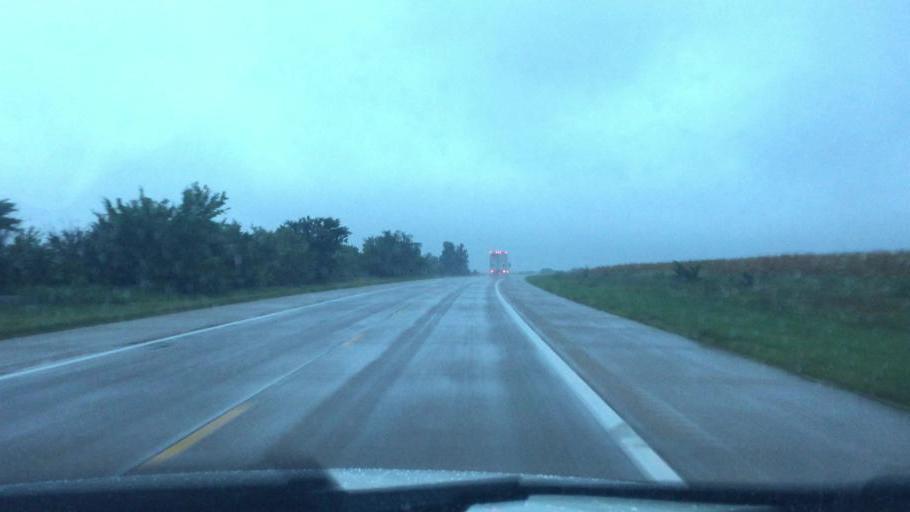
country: US
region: Kansas
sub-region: Neosho County
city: Chanute
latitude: 37.5380
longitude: -95.4708
